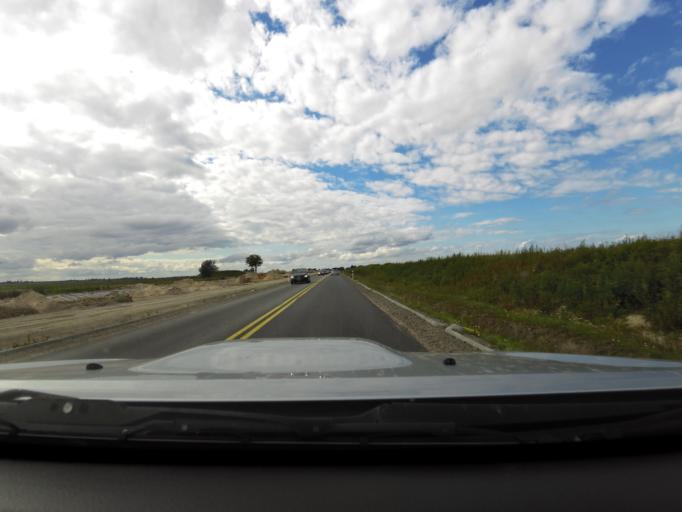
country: PL
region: Pomeranian Voivodeship
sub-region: Powiat nowodworski
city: Nowy Dwor Gdanski
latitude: 54.2307
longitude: 19.0489
